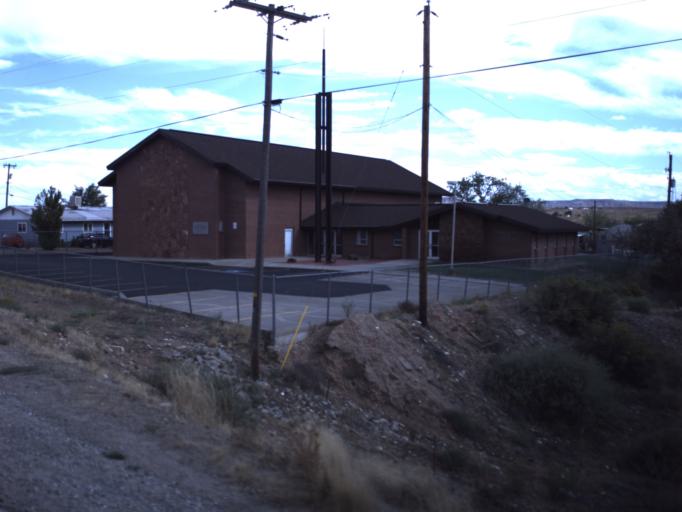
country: US
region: Utah
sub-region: San Juan County
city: Blanding
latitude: 37.2598
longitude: -109.3005
